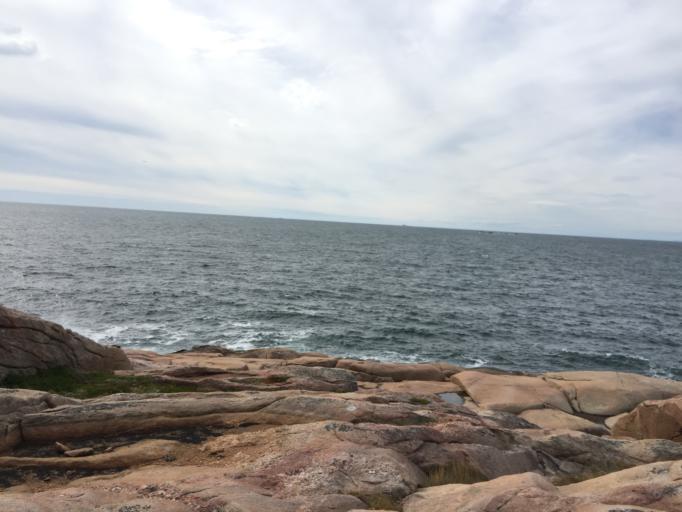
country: NO
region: Ostfold
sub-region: Hvaler
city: Skjaerhalden
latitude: 59.0321
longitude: 10.9438
